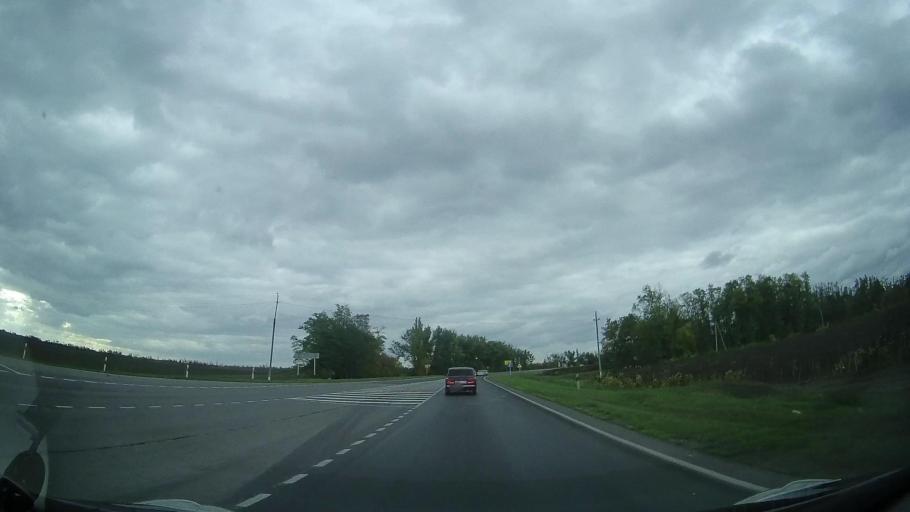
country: RU
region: Rostov
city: Yegorlykskaya
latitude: 46.5373
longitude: 40.7814
